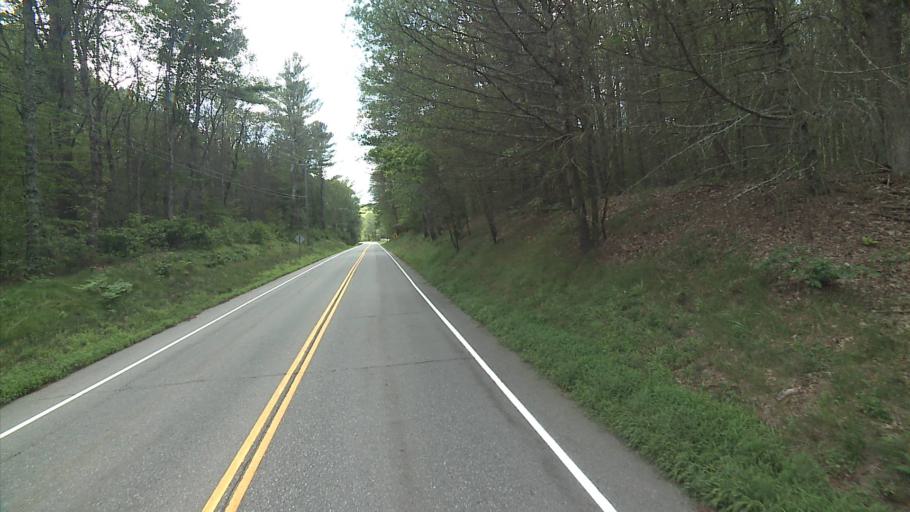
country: US
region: Connecticut
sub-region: Windham County
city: Windham
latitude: 41.8409
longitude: -72.0959
